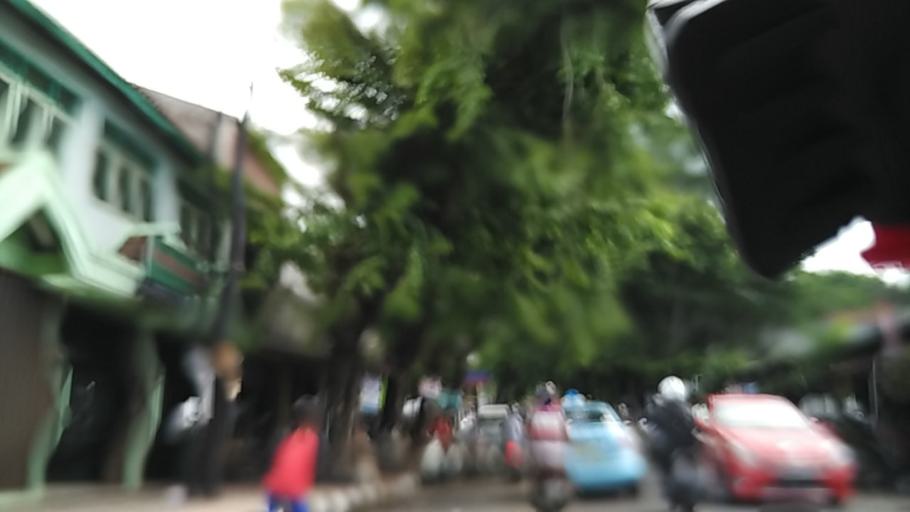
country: ID
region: Central Java
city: Semarang
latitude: -6.9879
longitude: 110.4140
